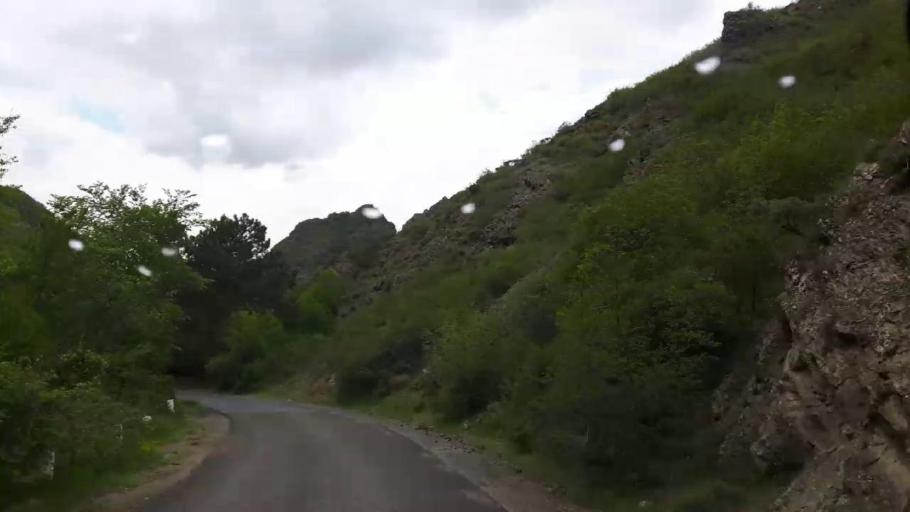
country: GE
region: Shida Kartli
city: Gori
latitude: 41.9000
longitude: 44.0676
